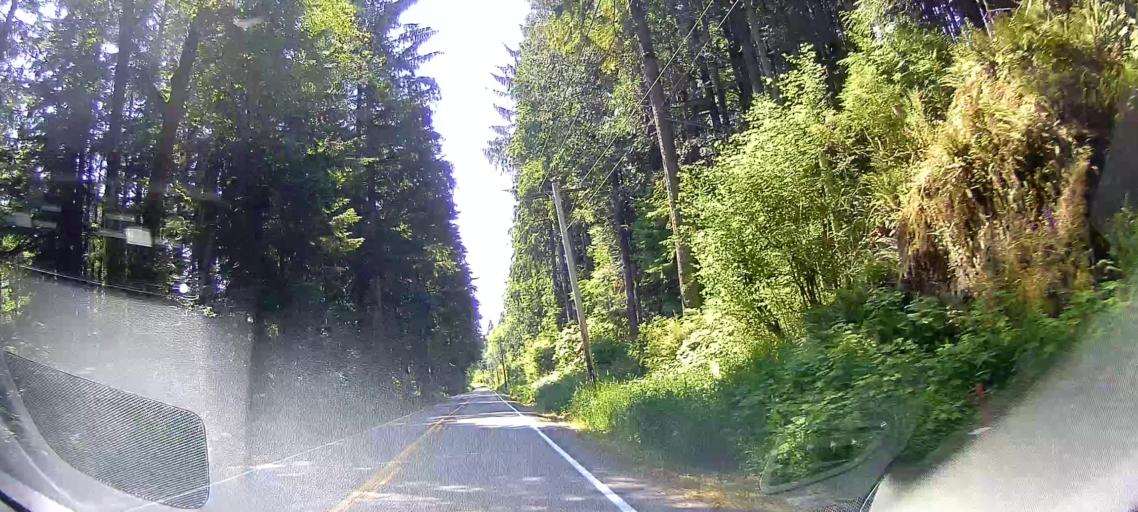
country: US
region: Washington
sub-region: Snohomish County
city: Bryant
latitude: 48.3443
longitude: -122.0747
